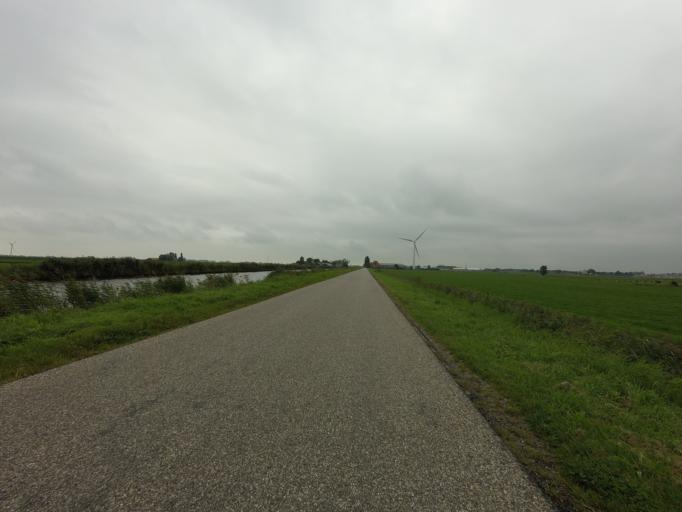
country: NL
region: Friesland
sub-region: Sudwest Fryslan
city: Workum
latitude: 52.9878
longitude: 5.4720
